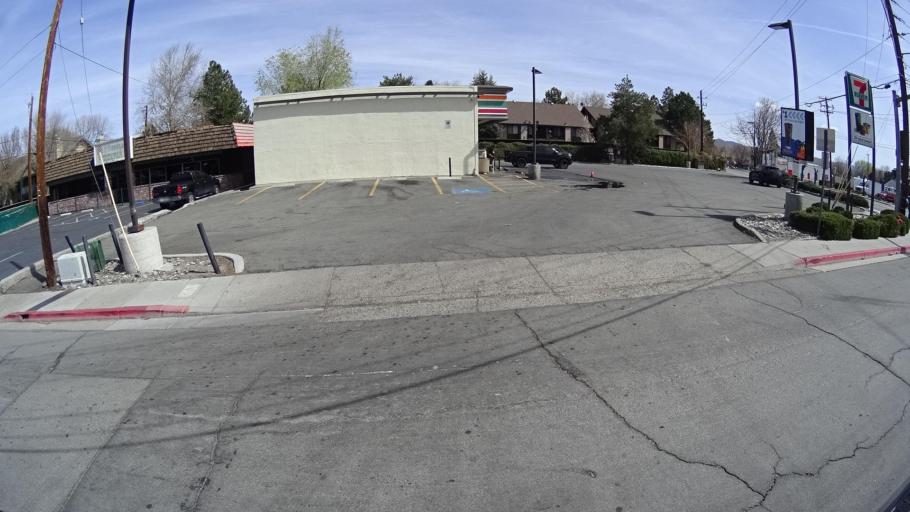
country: US
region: Nevada
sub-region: Washoe County
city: Reno
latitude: 39.4841
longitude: -119.7801
